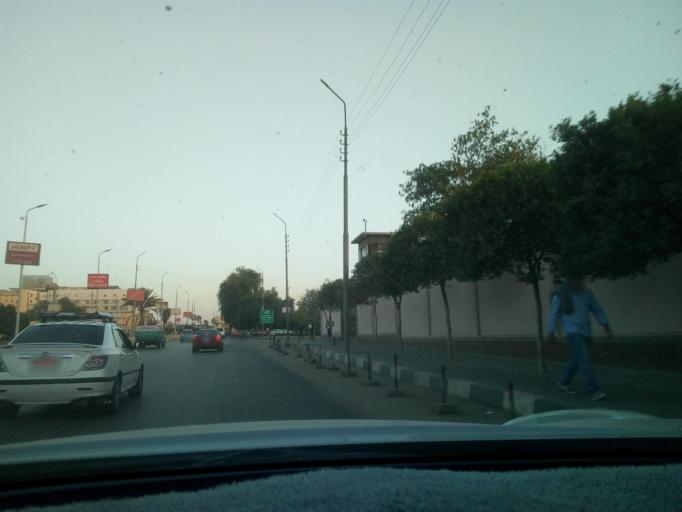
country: EG
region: Muhafazat al Qahirah
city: Cairo
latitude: 30.0936
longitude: 31.3450
